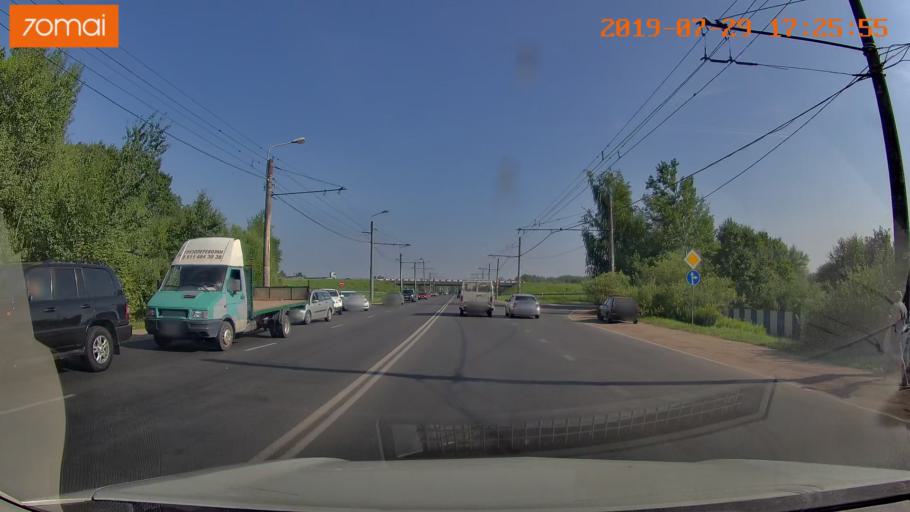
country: RU
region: Kaliningrad
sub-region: Gorod Kaliningrad
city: Kaliningrad
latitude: 54.7598
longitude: 20.4432
